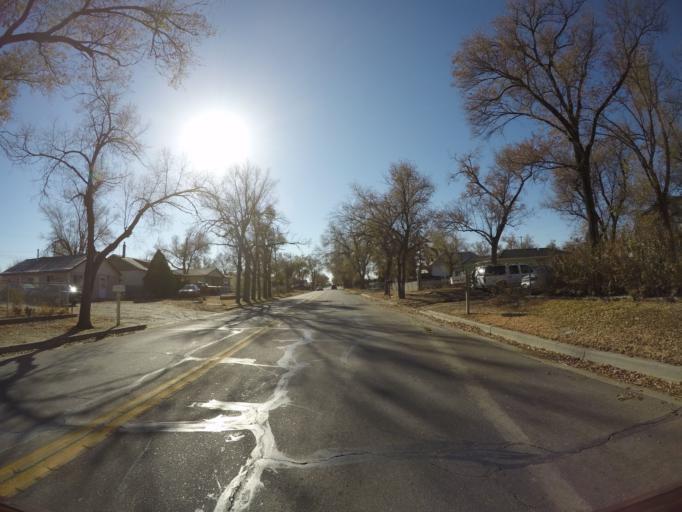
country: US
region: Colorado
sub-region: Otero County
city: La Junta
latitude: 37.9803
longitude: -103.5325
